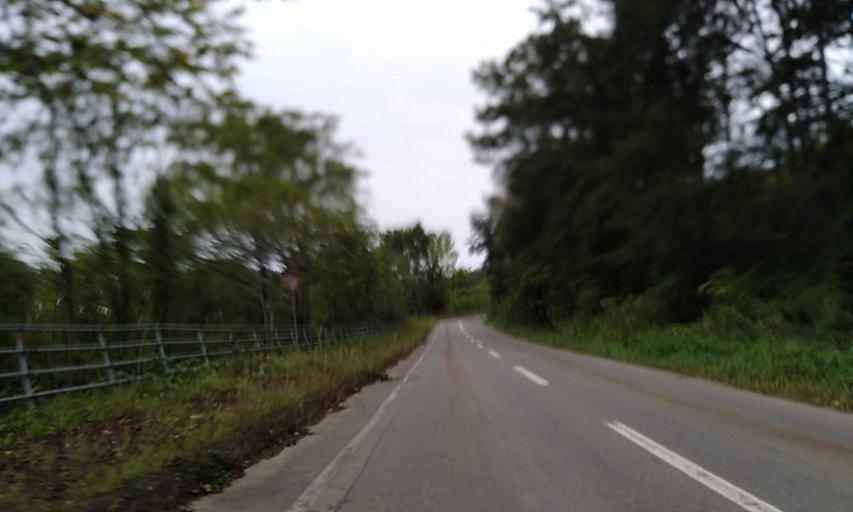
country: JP
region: Hokkaido
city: Obihiro
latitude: 42.6926
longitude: 143.0555
